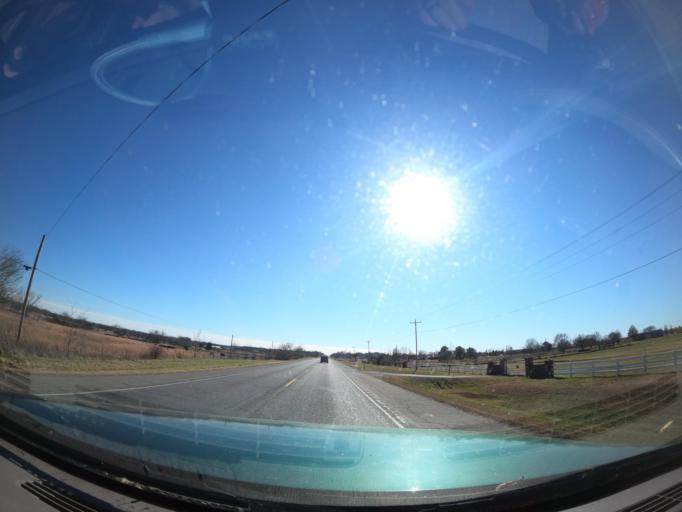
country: US
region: Oklahoma
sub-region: Muskogee County
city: Haskell
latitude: 35.8554
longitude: -95.6775
